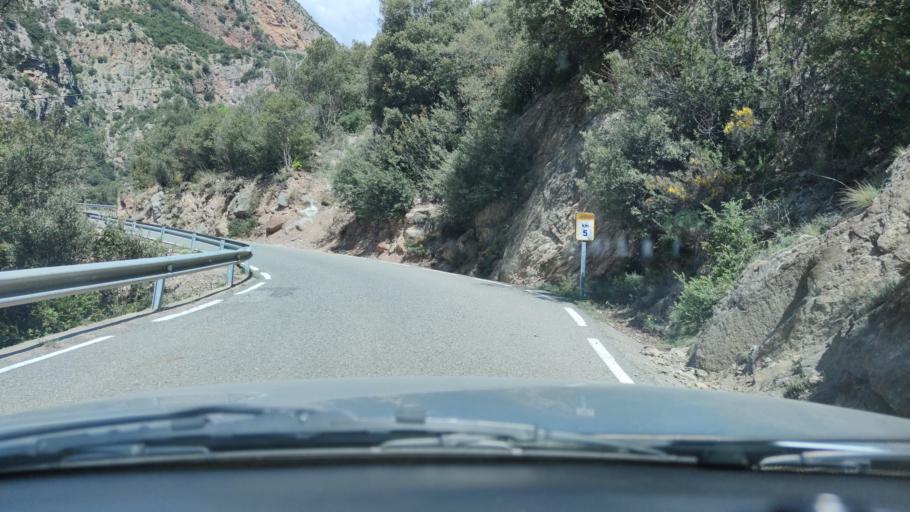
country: ES
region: Catalonia
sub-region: Provincia de Lleida
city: Coll de Nargo
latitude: 42.3003
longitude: 1.2955
